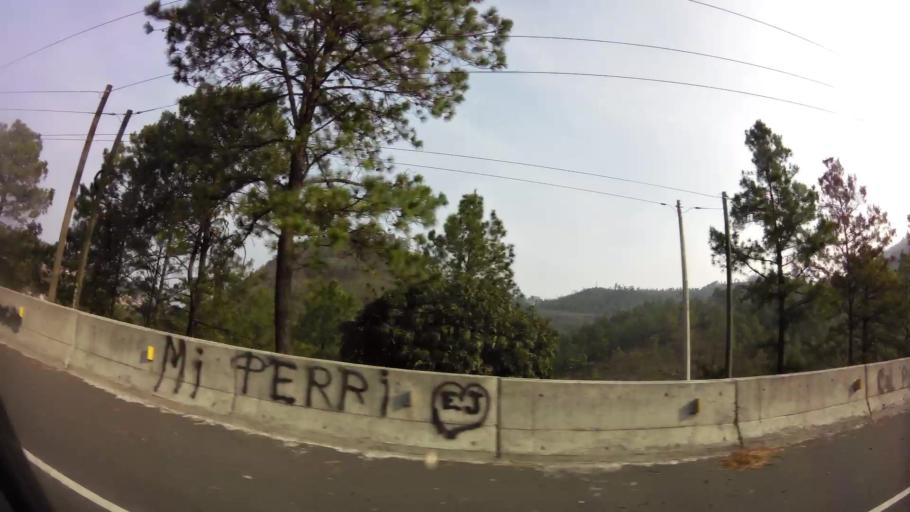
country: HN
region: Francisco Morazan
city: Zambrano
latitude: 14.2894
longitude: -87.4734
